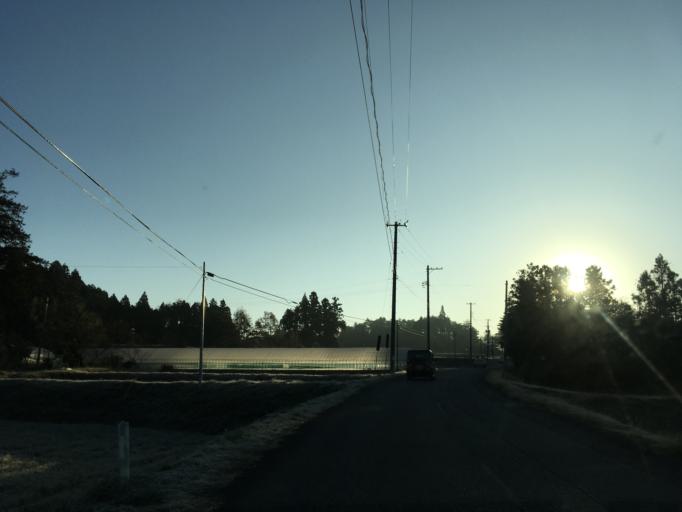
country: JP
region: Iwate
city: Ichinoseki
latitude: 38.7995
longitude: 141.2033
